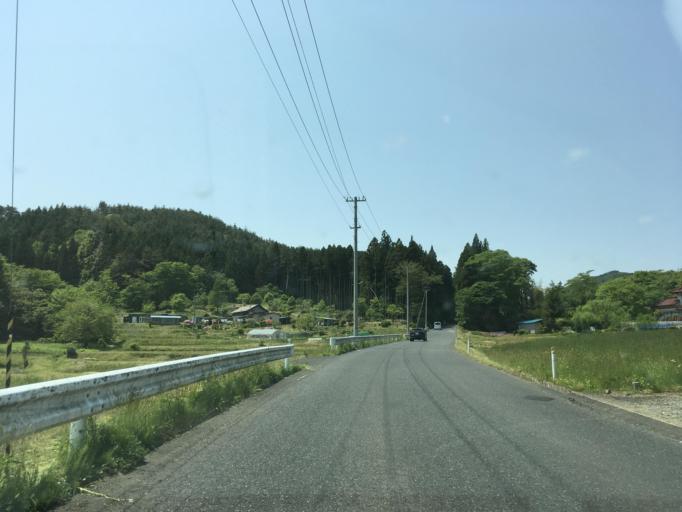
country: JP
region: Iwate
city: Ofunato
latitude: 38.8557
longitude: 141.5189
